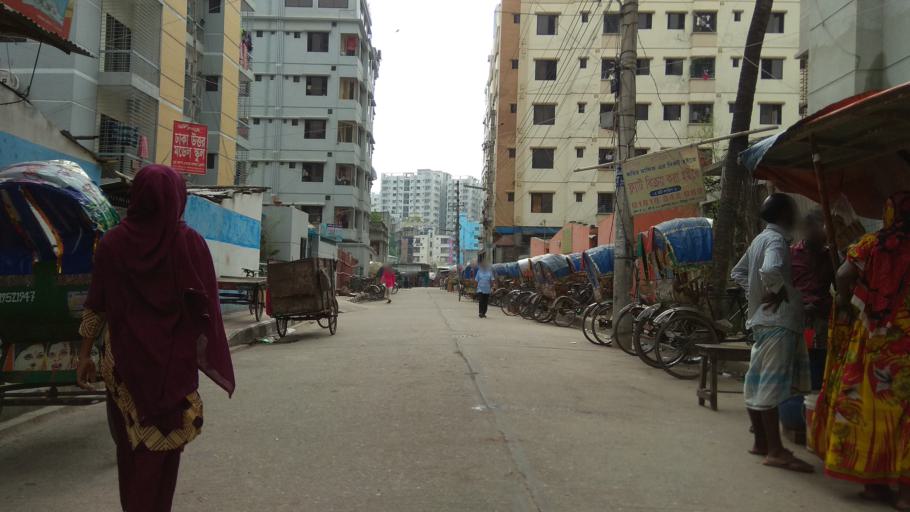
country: BD
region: Dhaka
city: Azimpur
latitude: 23.8126
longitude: 90.3568
